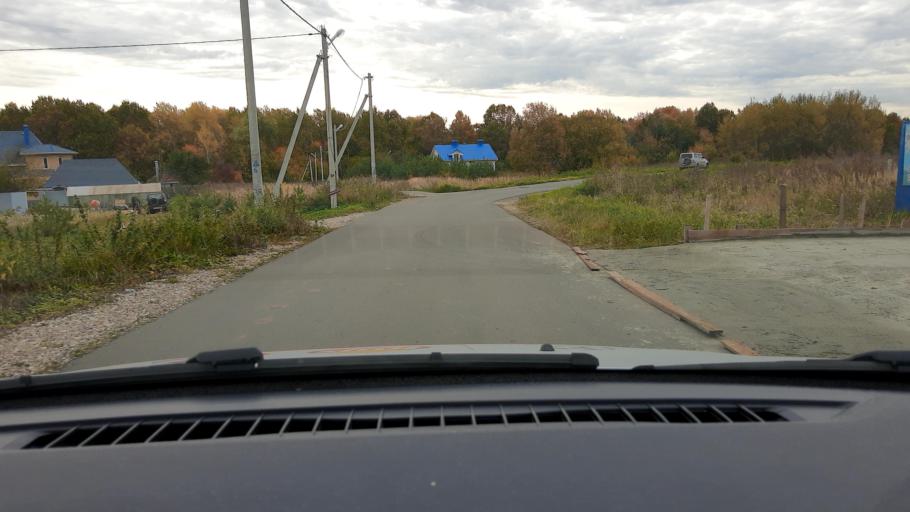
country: RU
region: Nizjnij Novgorod
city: Babino
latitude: 56.1288
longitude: 43.6477
